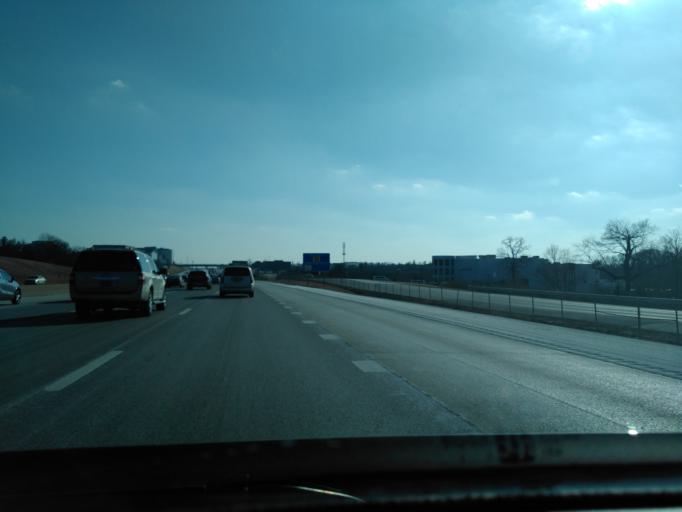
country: US
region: Missouri
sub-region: Saint Louis County
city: Town and Country
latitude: 38.6153
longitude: -90.4521
